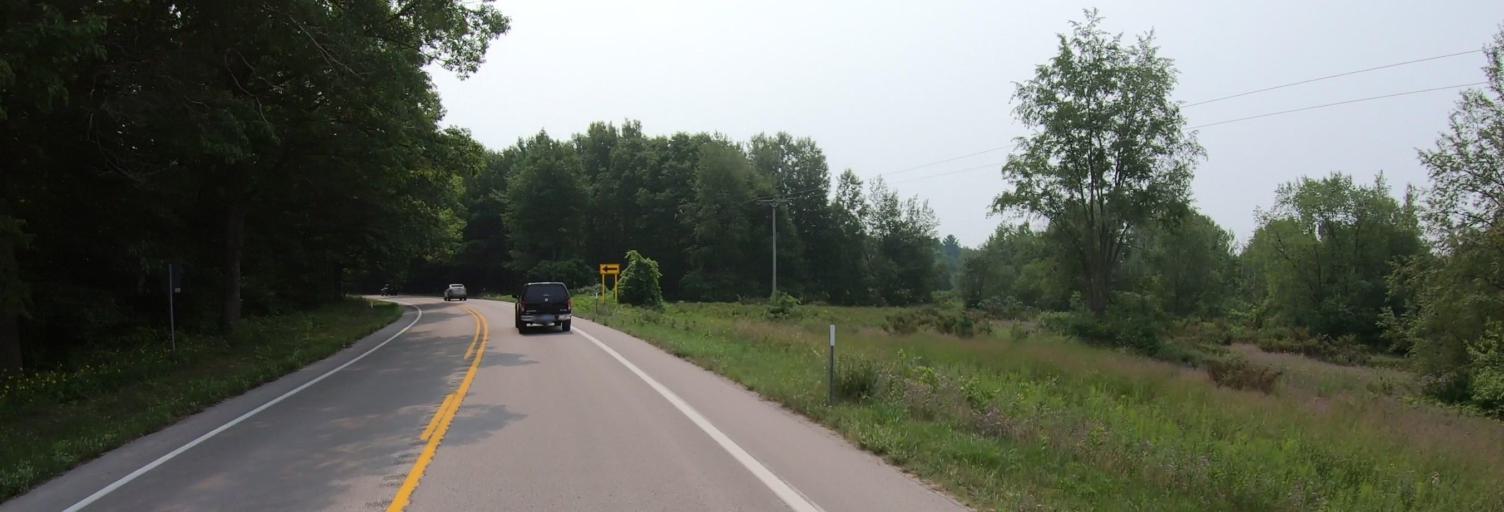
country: US
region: Michigan
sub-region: Leelanau County
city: Leland
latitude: 44.9230
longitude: -85.8795
